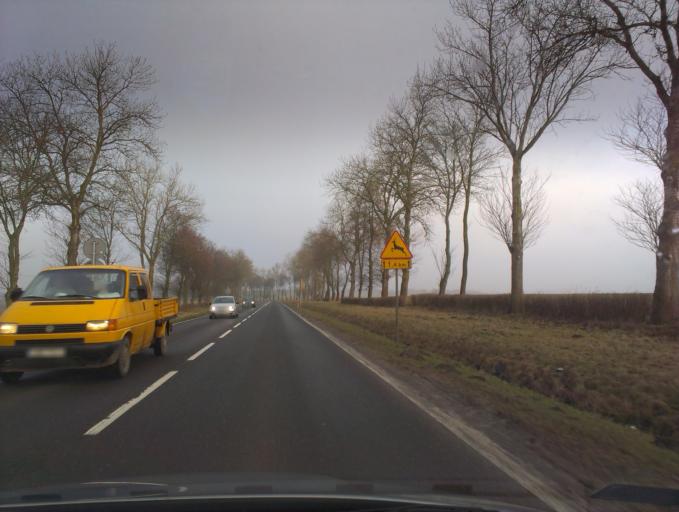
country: PL
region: West Pomeranian Voivodeship
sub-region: Koszalin
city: Koszalin
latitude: 54.1503
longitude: 16.2434
